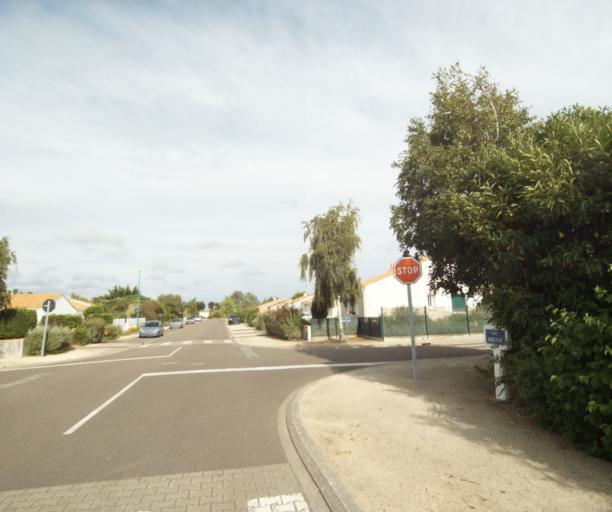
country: FR
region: Pays de la Loire
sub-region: Departement de la Vendee
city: Chateau-d'Olonne
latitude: 46.4880
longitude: -1.7355
